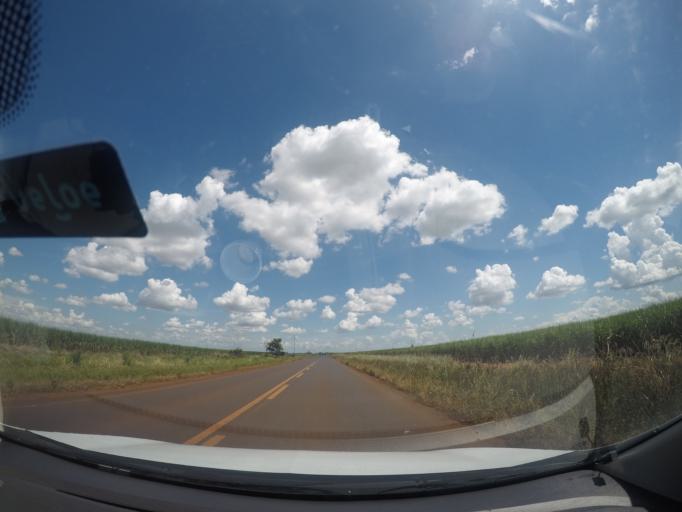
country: BR
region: Minas Gerais
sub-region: Frutal
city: Frutal
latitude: -19.8220
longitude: -48.7322
